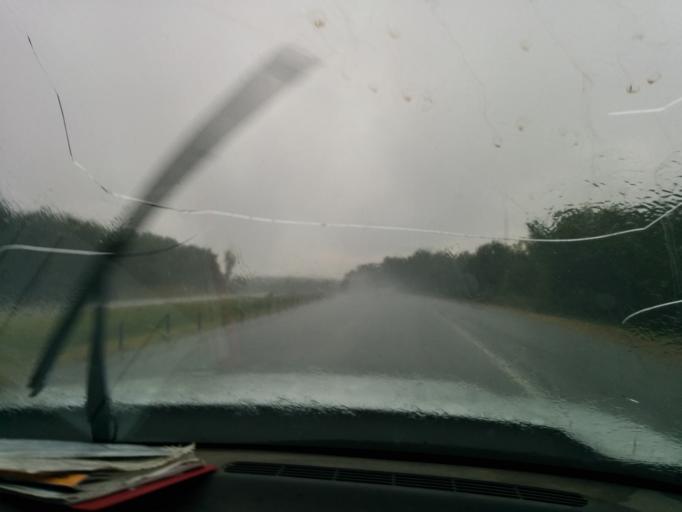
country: US
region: Oklahoma
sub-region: Okmulgee County
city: Beggs
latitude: 35.7324
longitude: -96.0046
